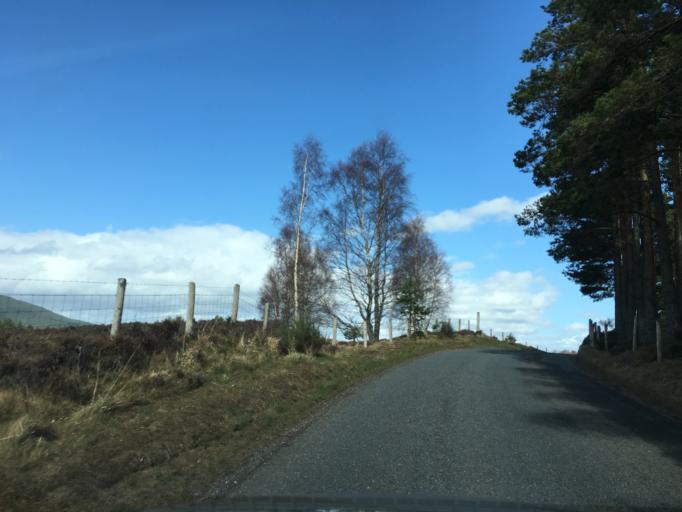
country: GB
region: Scotland
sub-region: Highland
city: Aviemore
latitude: 57.2006
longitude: -3.7983
